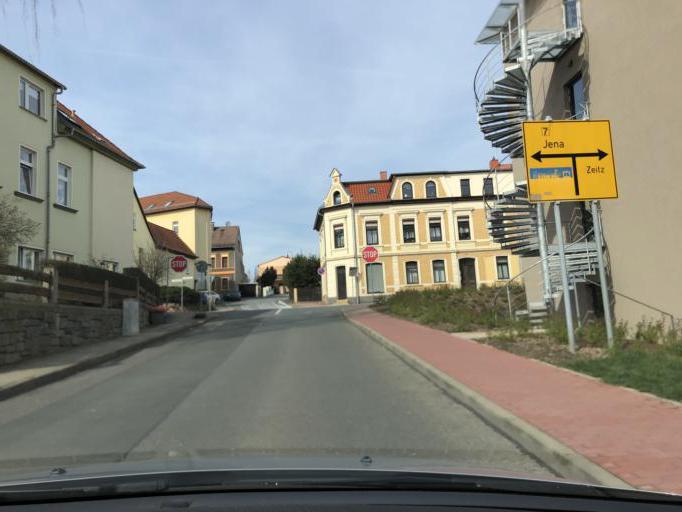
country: DE
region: Thuringia
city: Eisenberg
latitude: 50.9708
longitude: 11.9004
